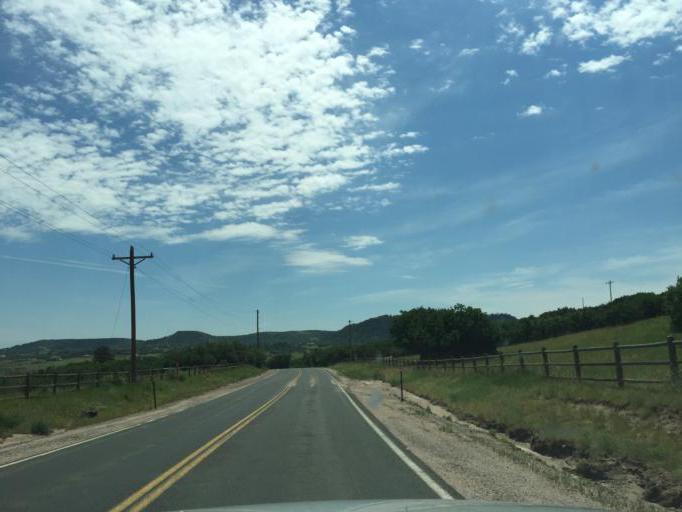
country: US
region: Colorado
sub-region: Douglas County
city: Castle Rock
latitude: 39.2982
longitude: -104.9017
